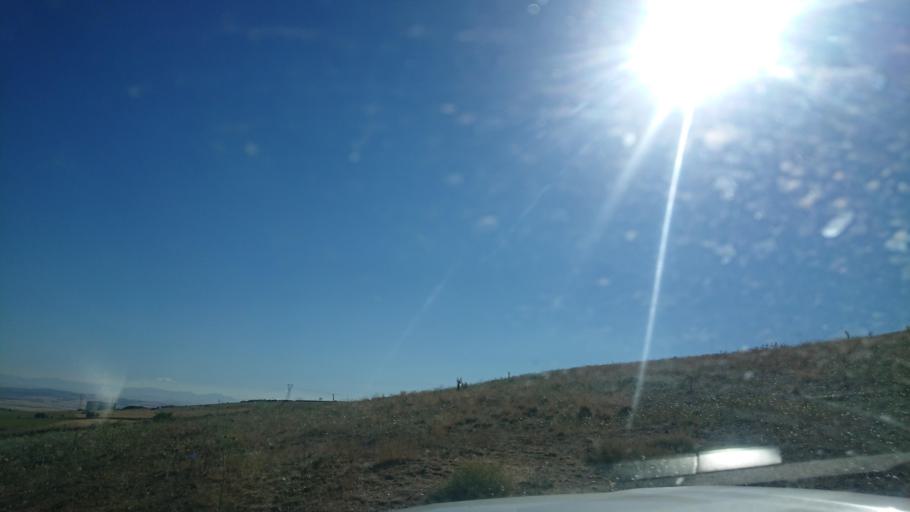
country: TR
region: Aksaray
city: Agacoren
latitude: 38.8387
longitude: 33.9367
